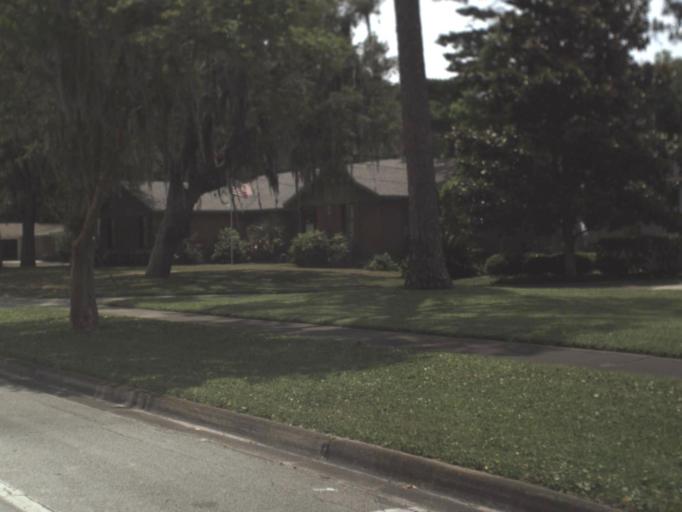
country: US
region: Florida
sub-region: Nassau County
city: Fernandina Beach
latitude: 30.6693
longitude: -81.4462
